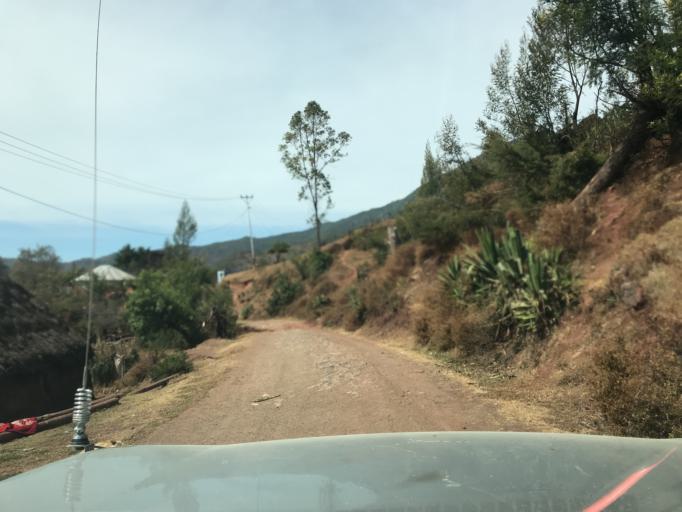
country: TL
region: Ainaro
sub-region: Ainaro
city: Ainaro
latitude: -8.8844
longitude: 125.5222
